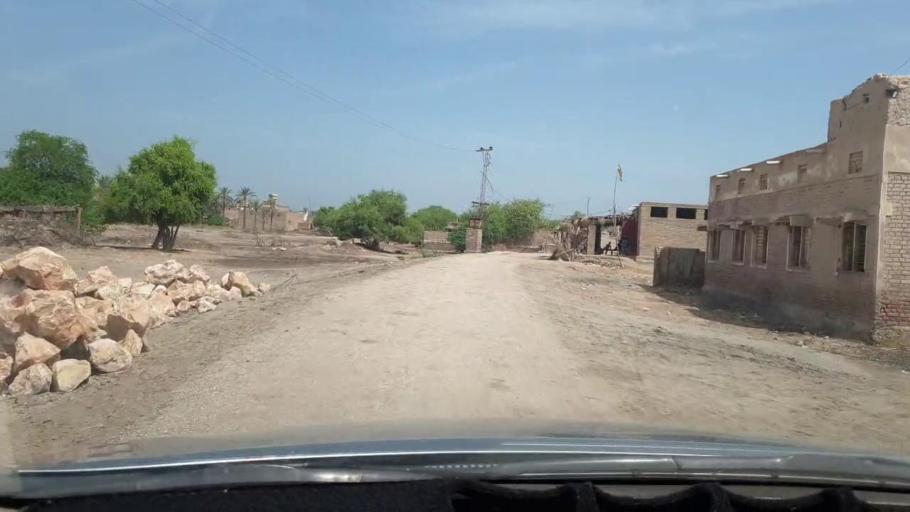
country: PK
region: Sindh
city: Khairpur
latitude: 27.4735
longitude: 68.7414
